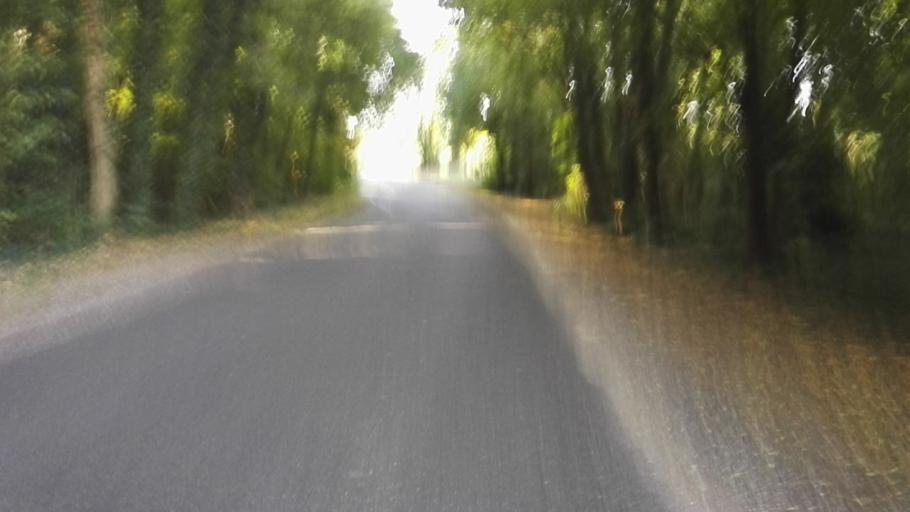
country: FR
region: Haute-Normandie
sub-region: Departement de l'Eure
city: Menilles
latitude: 49.0502
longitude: 1.3361
